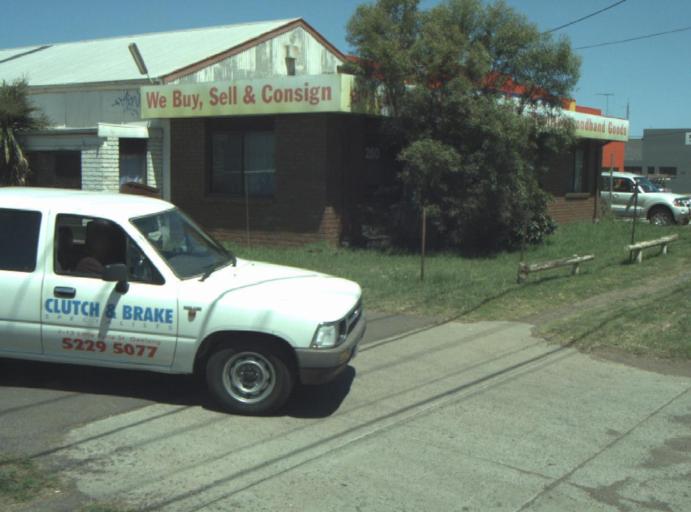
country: AU
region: Victoria
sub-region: Greater Geelong
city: Bell Park
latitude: -38.1090
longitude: 144.3438
